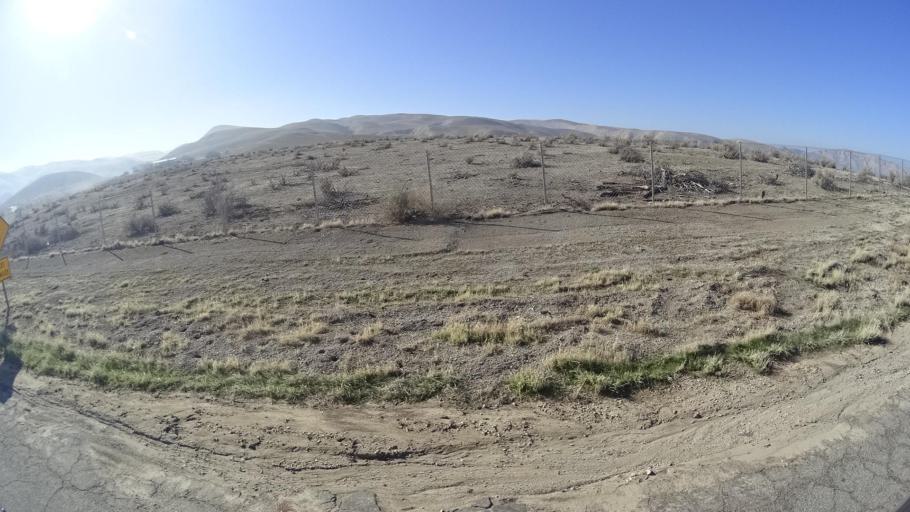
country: US
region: California
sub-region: Kern County
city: Maricopa
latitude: 34.9923
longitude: -119.3917
